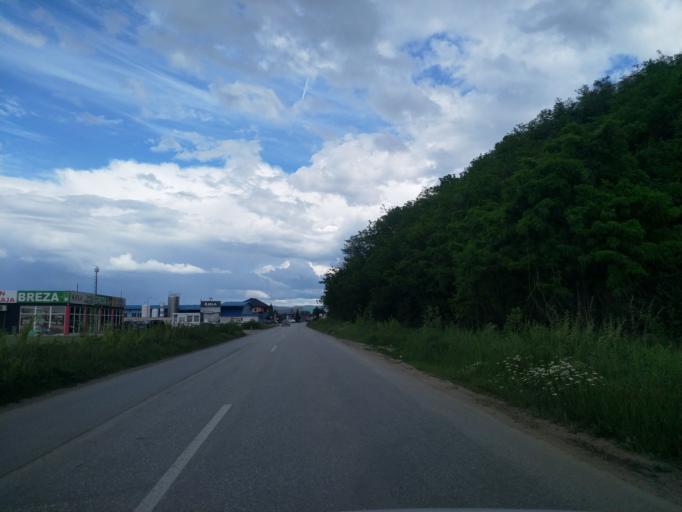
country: RS
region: Central Serbia
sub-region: Pomoravski Okrug
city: Jagodina
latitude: 43.9542
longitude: 21.3129
